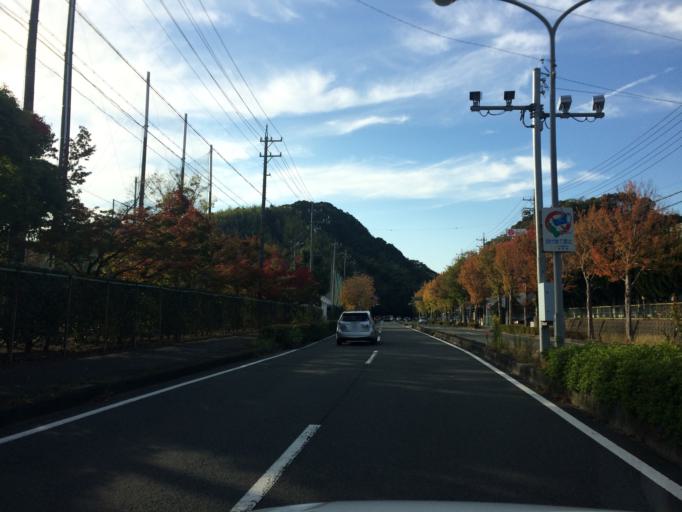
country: JP
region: Shizuoka
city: Fujieda
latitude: 34.8665
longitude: 138.2358
